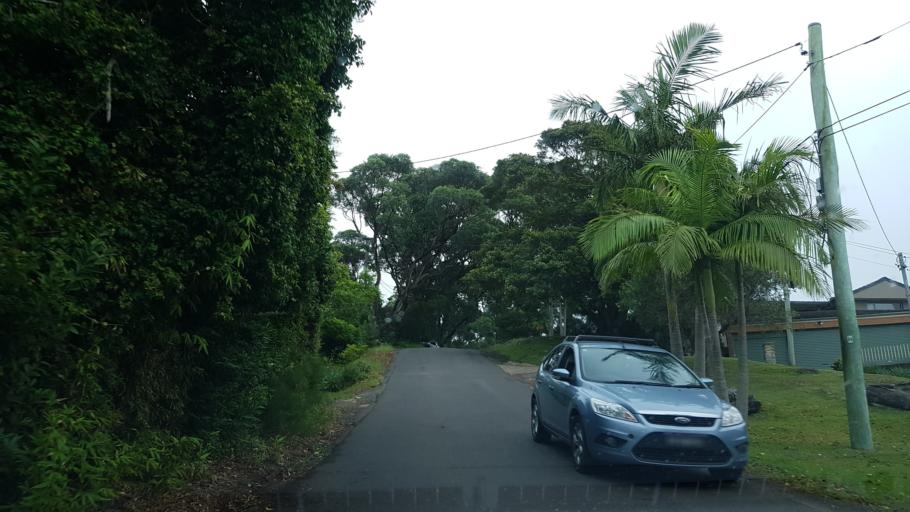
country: AU
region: New South Wales
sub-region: Pittwater
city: North Narrabeen
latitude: -33.7089
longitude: 151.2896
